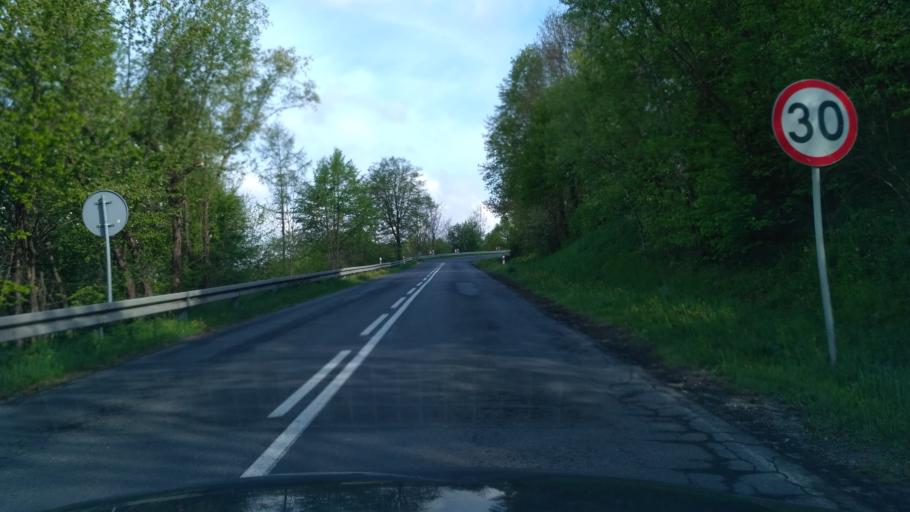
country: PL
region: Subcarpathian Voivodeship
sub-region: Powiat przeworski
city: Jawornik Polski
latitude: 49.8843
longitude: 22.2386
